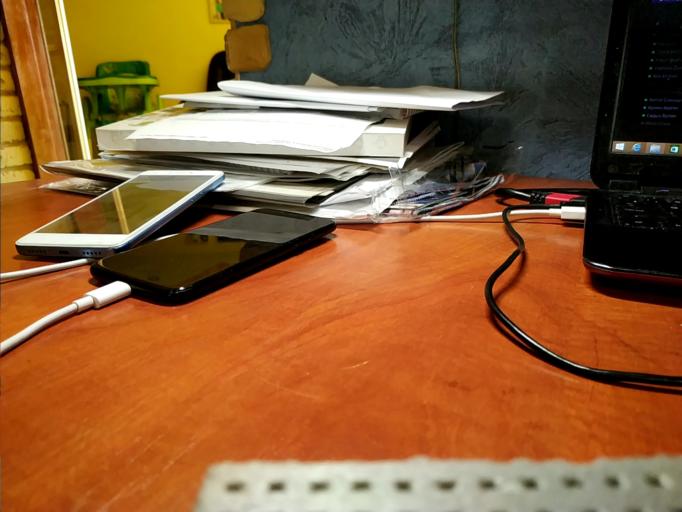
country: RU
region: Tverskaya
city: Spirovo
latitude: 57.4209
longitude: 35.1053
